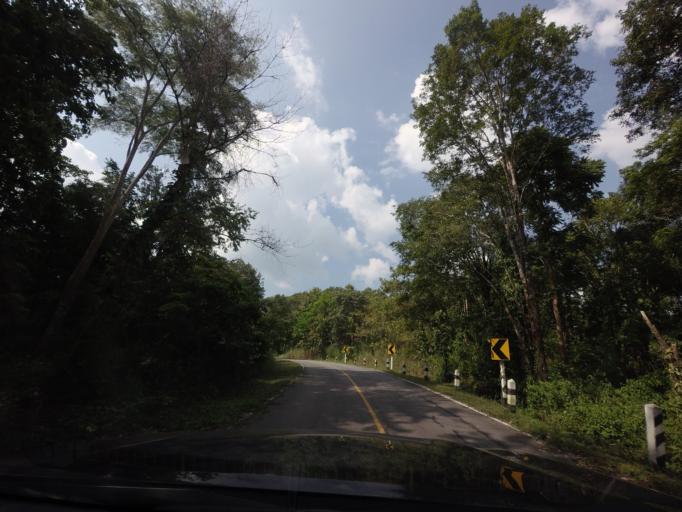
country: TH
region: Uttaradit
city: Ban Khok
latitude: 18.1602
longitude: 101.0872
